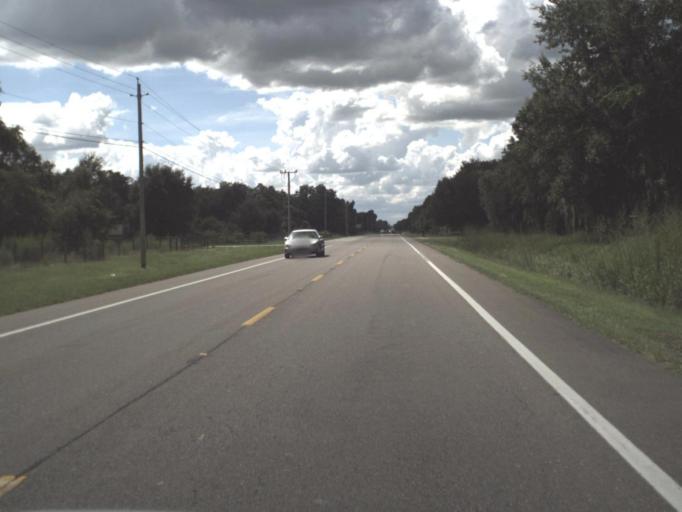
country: US
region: Florida
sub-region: Polk County
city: Highland City
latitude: 27.9968
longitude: -81.8641
